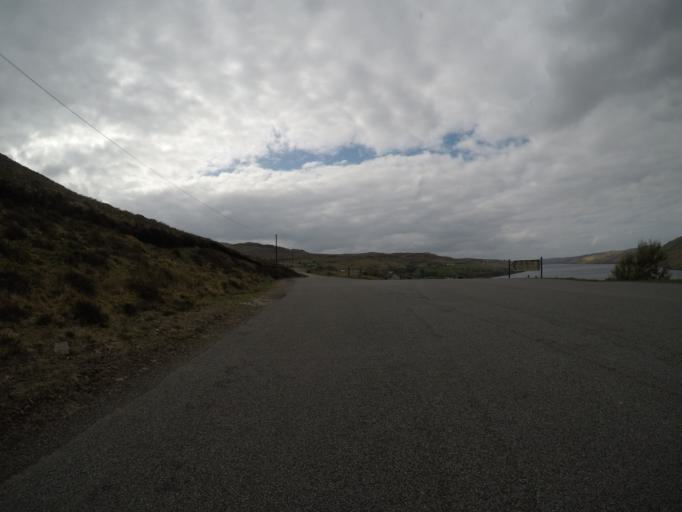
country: GB
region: Scotland
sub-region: Highland
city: Isle of Skye
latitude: 57.2969
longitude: -6.3434
